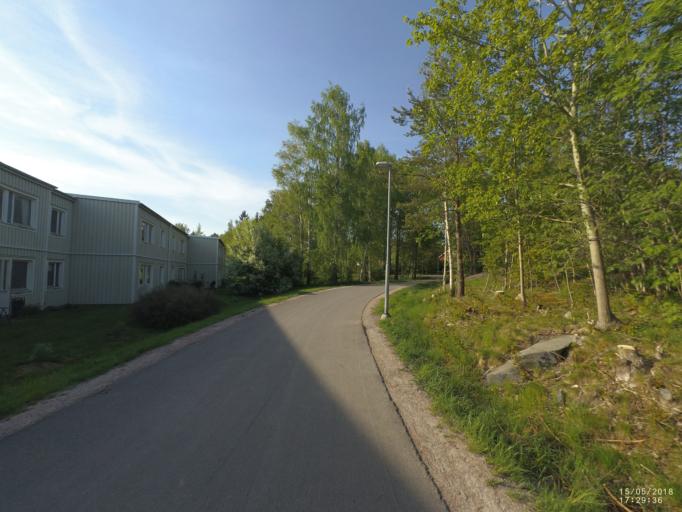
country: SE
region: Soedermanland
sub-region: Nykopings Kommun
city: Nykoping
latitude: 58.7292
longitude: 17.0207
